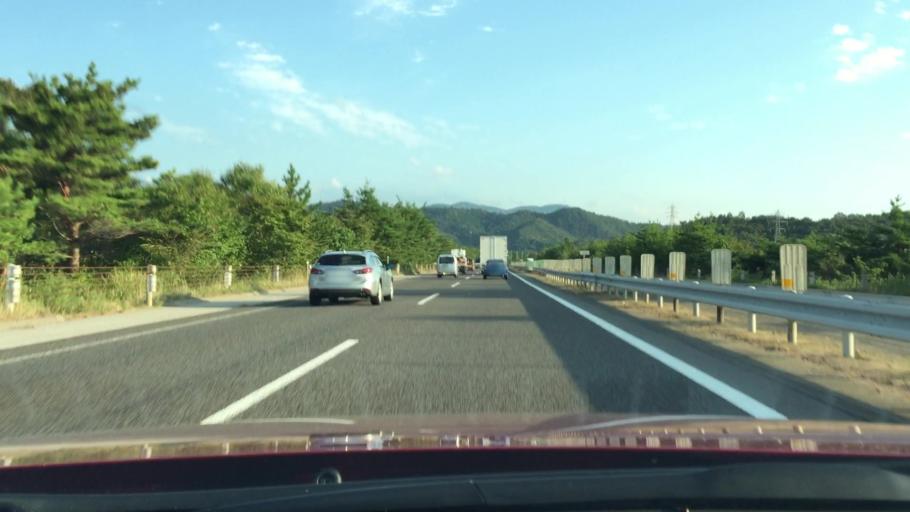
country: JP
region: Shiga Prefecture
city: Nagahama
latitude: 35.3653
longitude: 136.3059
